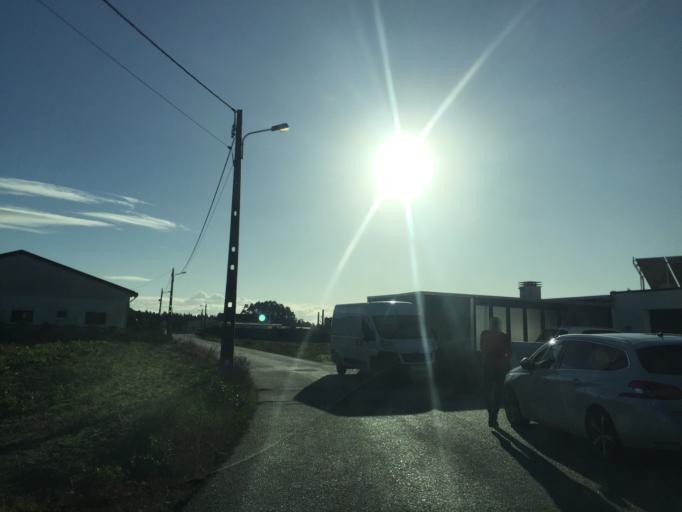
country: PT
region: Coimbra
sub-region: Figueira da Foz
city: Lavos
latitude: 40.0546
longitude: -8.8137
